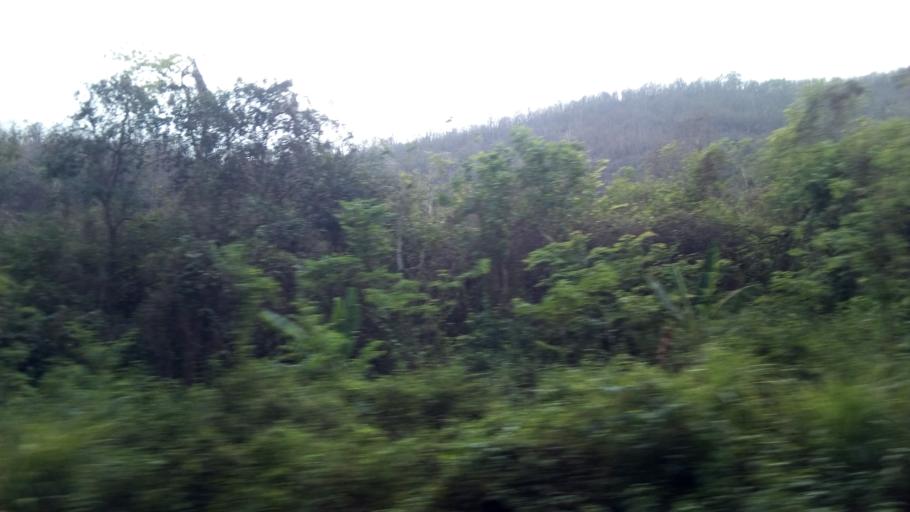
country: TH
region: Sara Buri
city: Saraburi
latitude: 14.4485
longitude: 100.9551
